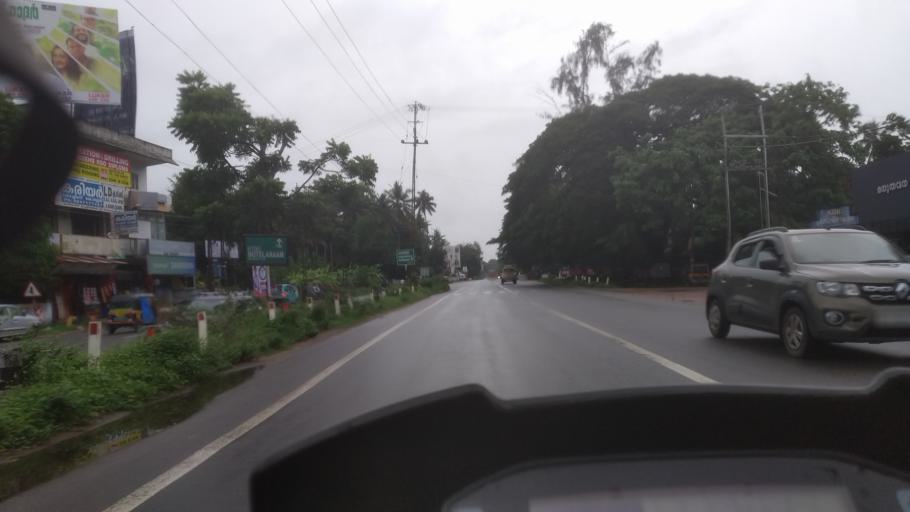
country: IN
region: Kerala
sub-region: Alappuzha
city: Kayankulam
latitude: 9.1387
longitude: 76.5121
